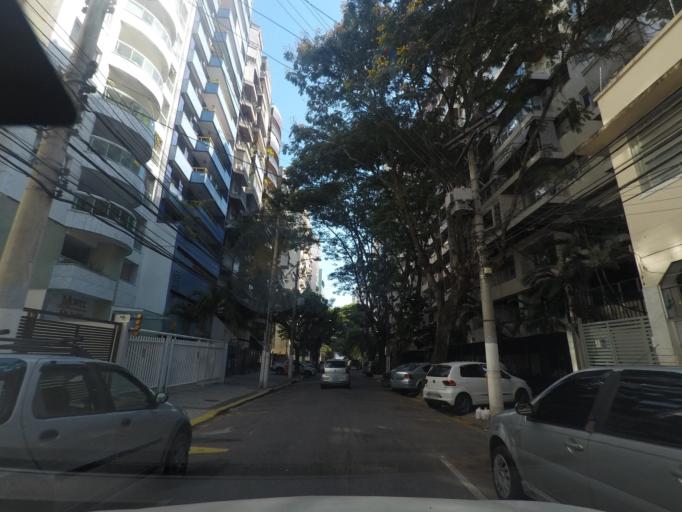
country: BR
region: Rio de Janeiro
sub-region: Niteroi
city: Niteroi
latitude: -22.9019
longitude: -43.1228
